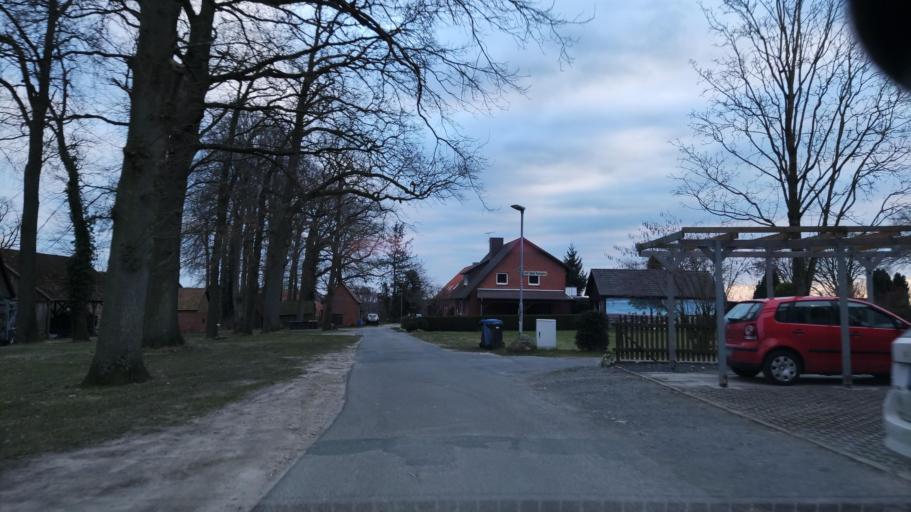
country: DE
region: Lower Saxony
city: Barum
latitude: 53.0464
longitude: 10.5456
